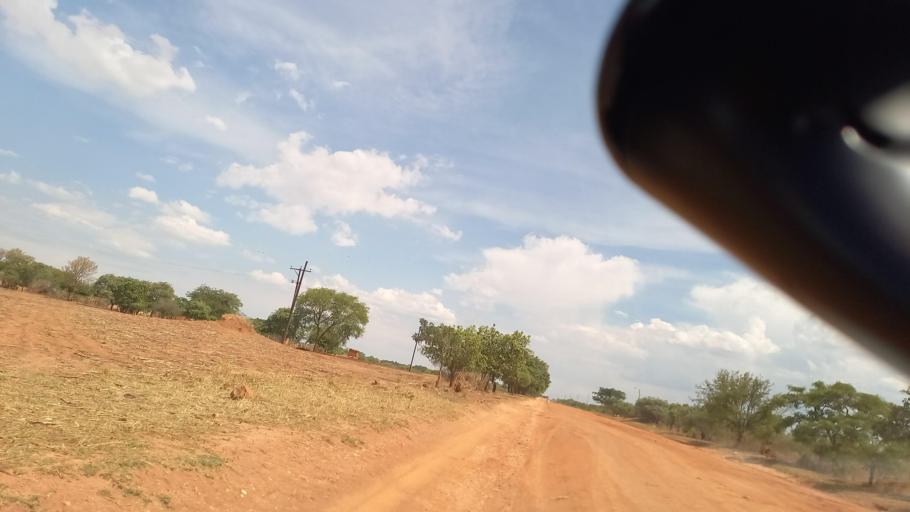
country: ZM
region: Lusaka
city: Kafue
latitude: -16.1368
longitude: 28.0510
